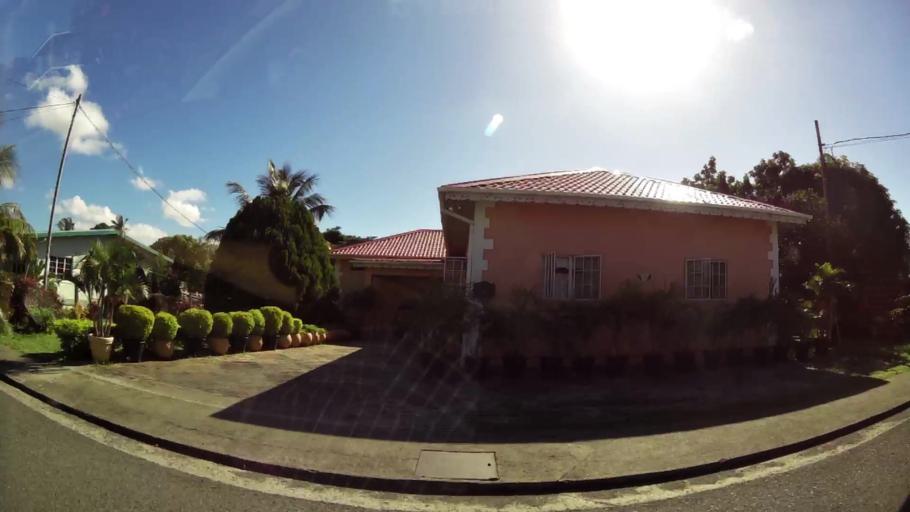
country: TT
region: Tobago
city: Scarborough
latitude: 11.1610
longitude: -60.8105
